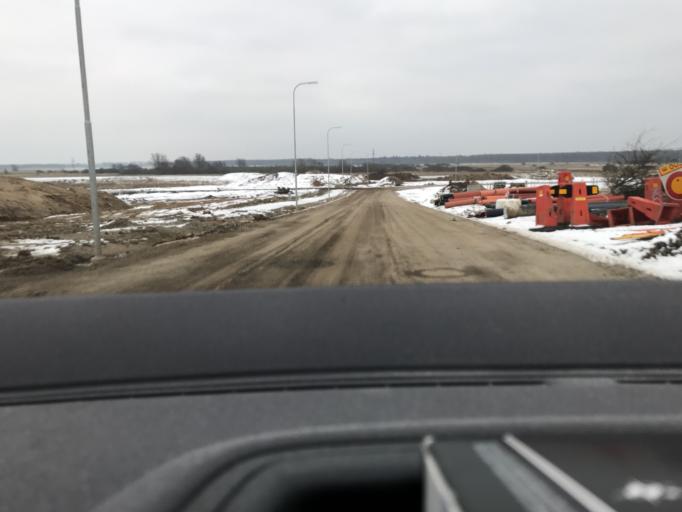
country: SE
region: Skane
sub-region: Ystads Kommun
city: Ystad
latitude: 55.4498
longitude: 13.8537
